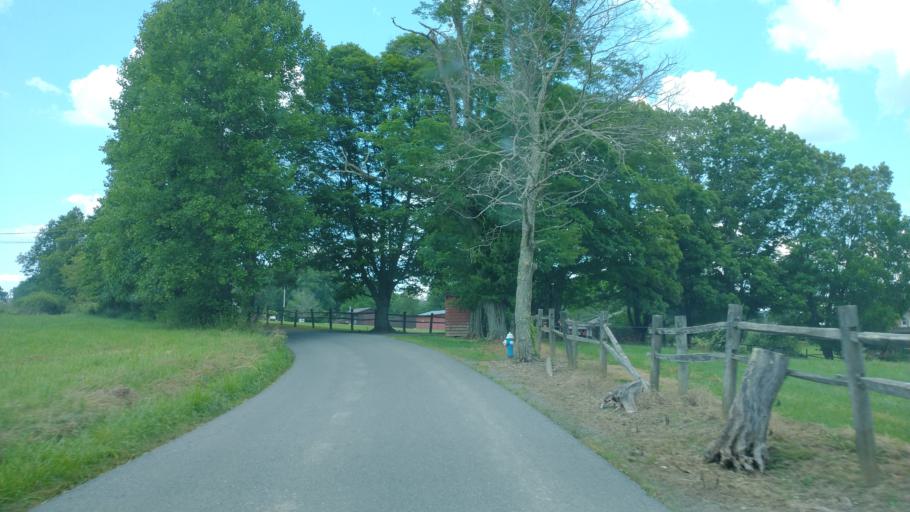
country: US
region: West Virginia
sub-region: Mercer County
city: Athens
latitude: 37.4560
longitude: -81.0282
